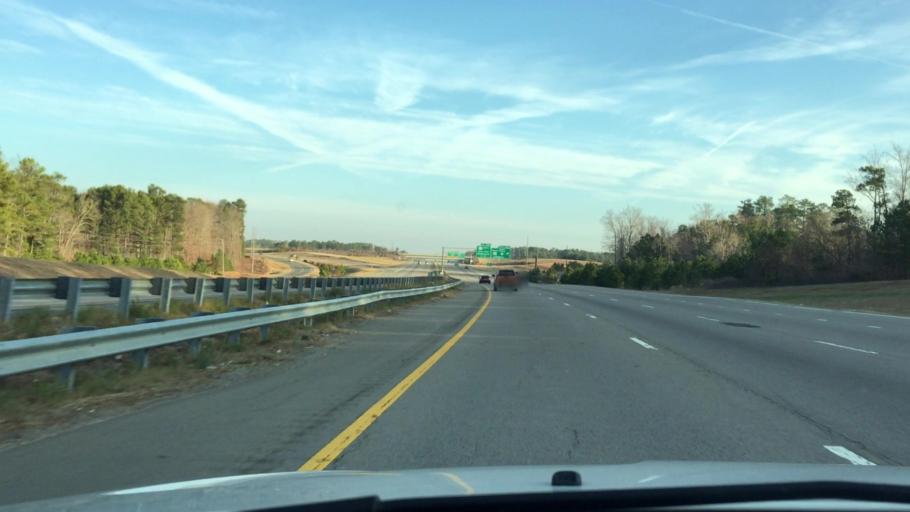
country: US
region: North Carolina
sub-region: Lee County
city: Sanford
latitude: 35.5039
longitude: -79.1905
